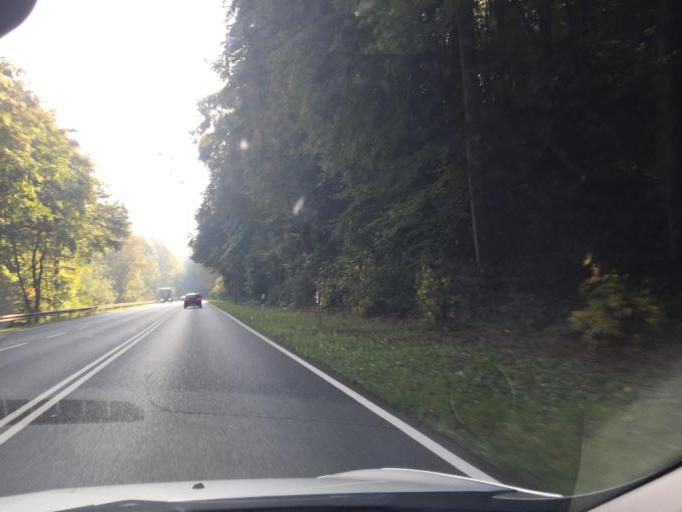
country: LU
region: Luxembourg
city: Schrassig
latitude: 49.6012
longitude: 6.2390
